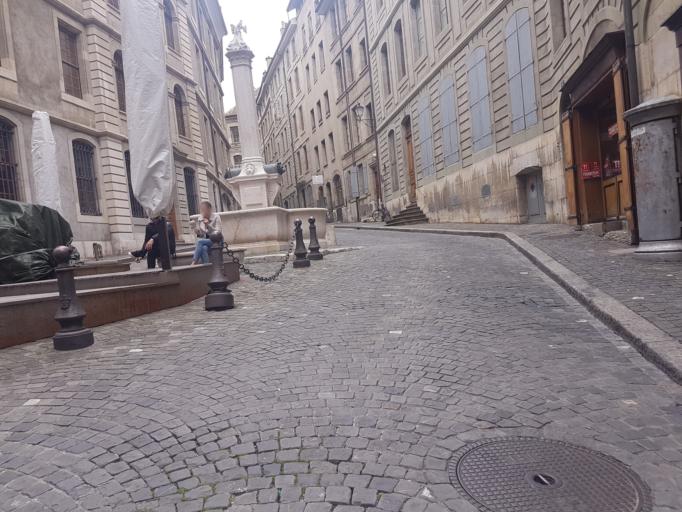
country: CH
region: Geneva
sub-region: Geneva
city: Geneve
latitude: 46.2024
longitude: 6.1445
